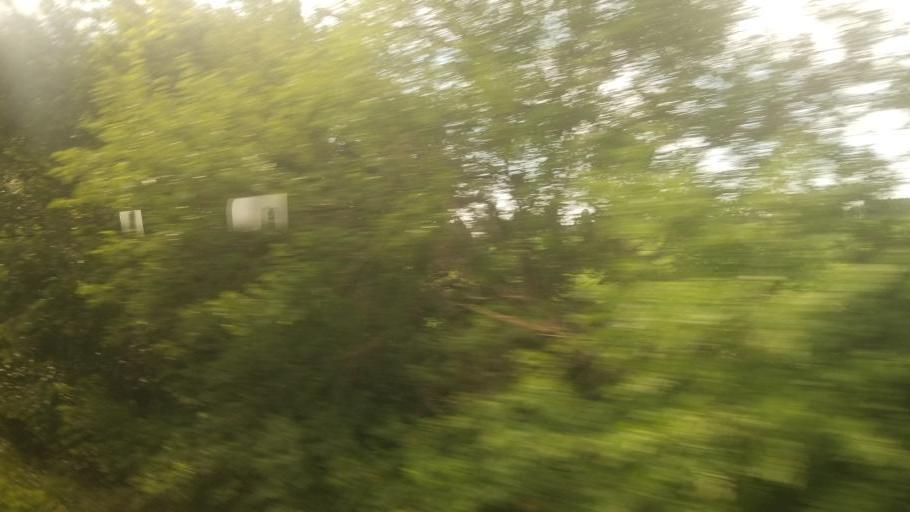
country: US
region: Kansas
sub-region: Douglas County
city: Eudora
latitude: 38.9499
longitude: -95.1628
